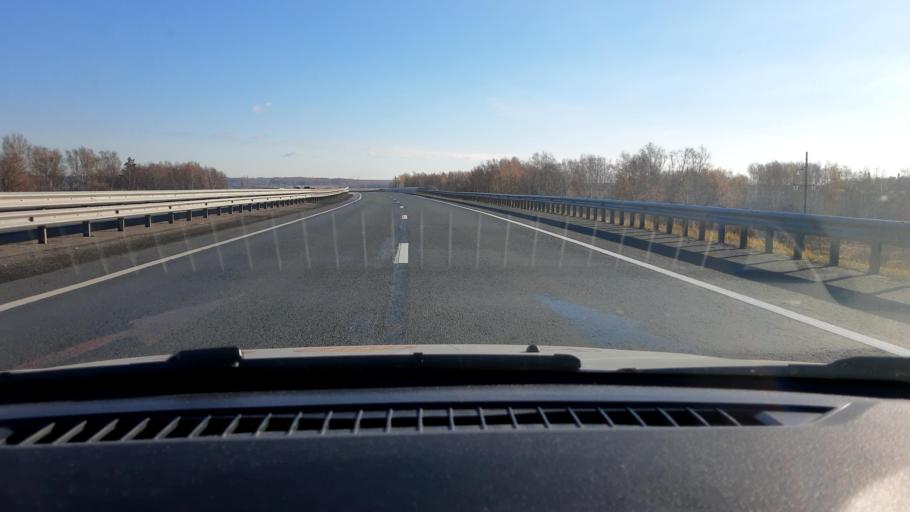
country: RU
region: Nizjnij Novgorod
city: Burevestnik
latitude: 56.1142
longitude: 43.8322
